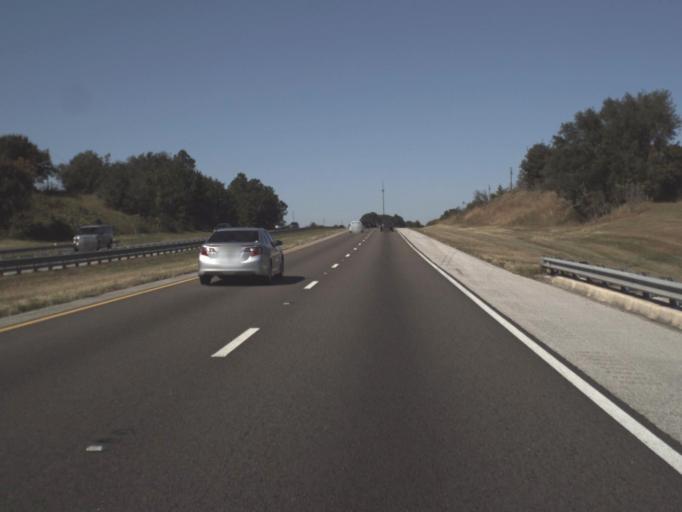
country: US
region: Florida
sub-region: Lake County
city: Minneola
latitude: 28.6318
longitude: -81.7708
